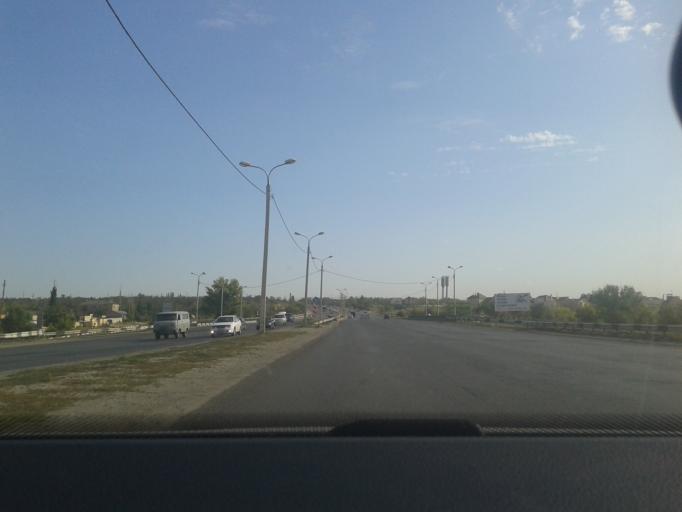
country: RU
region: Volgograd
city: Volgograd
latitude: 48.7308
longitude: 44.4520
